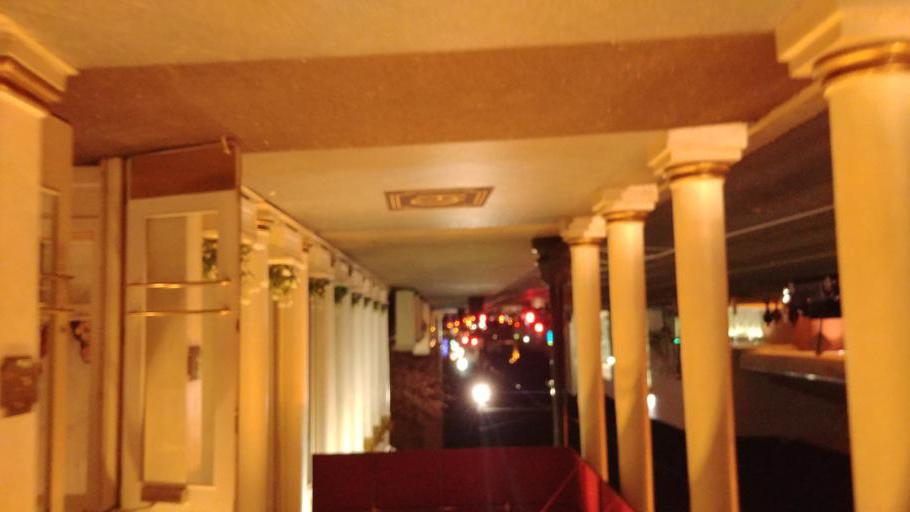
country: US
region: Arkansas
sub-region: Pulaski County
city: Little Rock
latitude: 34.7482
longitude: -92.2713
